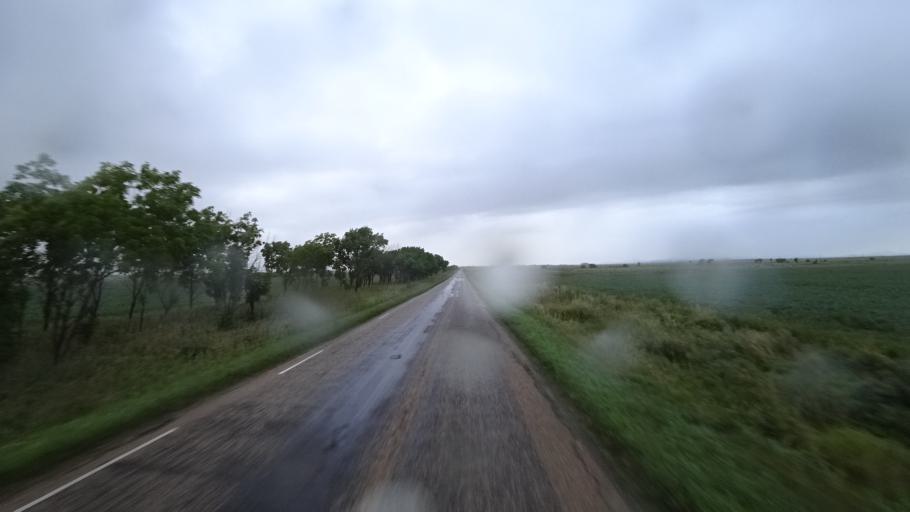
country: RU
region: Primorskiy
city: Chernigovka
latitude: 44.3777
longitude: 132.5297
